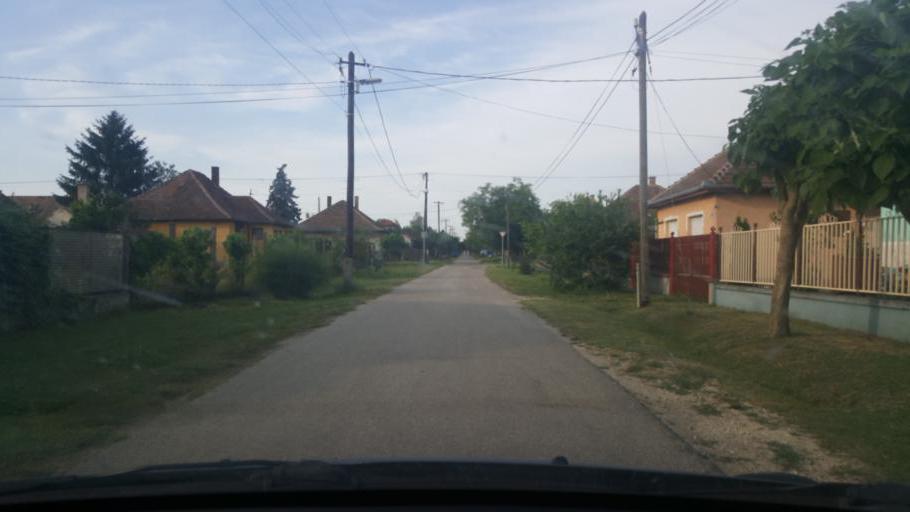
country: HU
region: Pest
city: Monor
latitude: 47.3366
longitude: 19.4506
